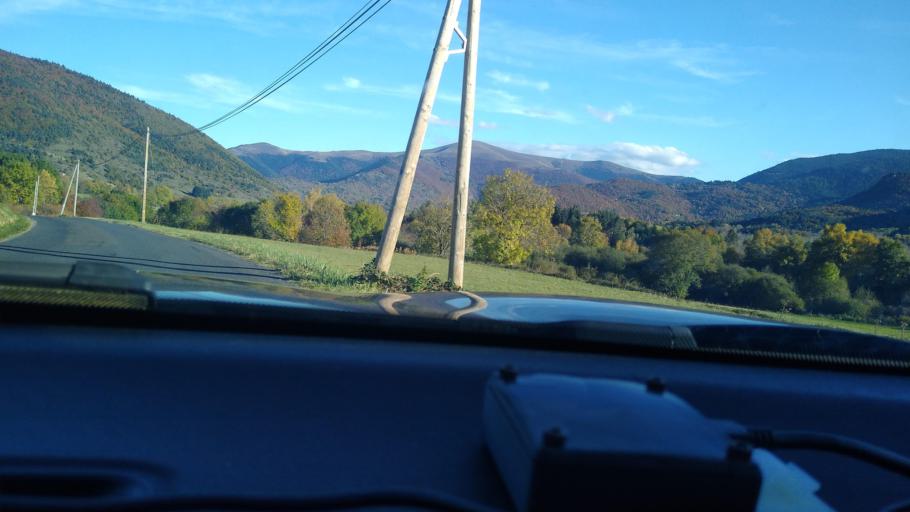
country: FR
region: Languedoc-Roussillon
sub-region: Departement de l'Aude
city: Quillan
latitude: 42.7458
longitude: 2.1781
